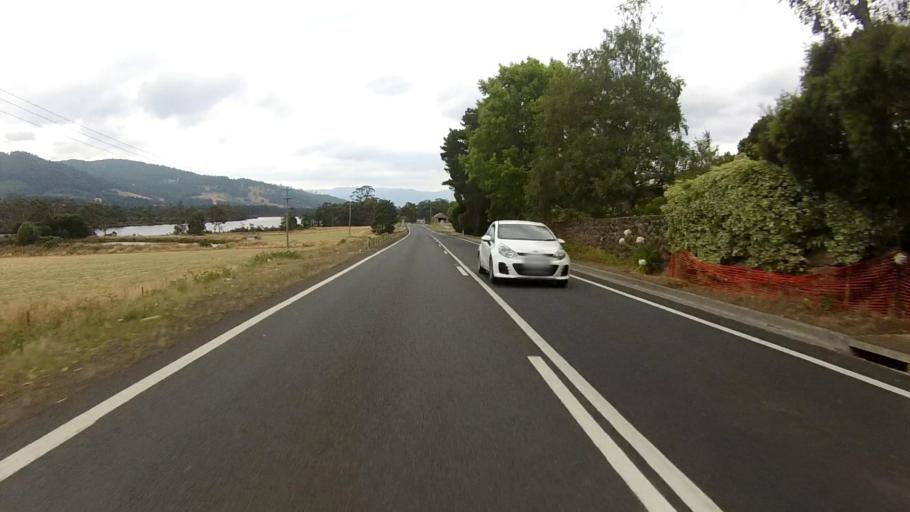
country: AU
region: Tasmania
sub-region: Huon Valley
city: Franklin
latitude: -43.0852
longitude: 147.0298
